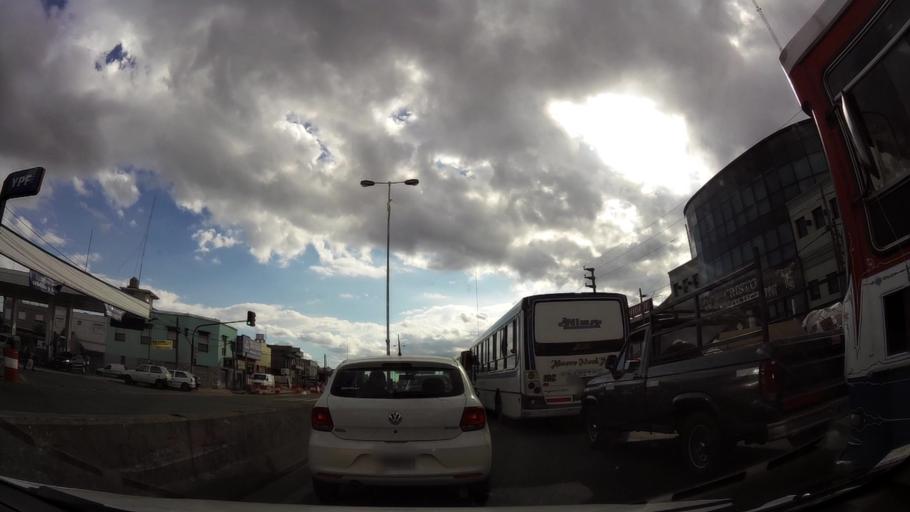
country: AR
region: Buenos Aires
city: San Justo
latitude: -34.6864
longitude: -58.5622
